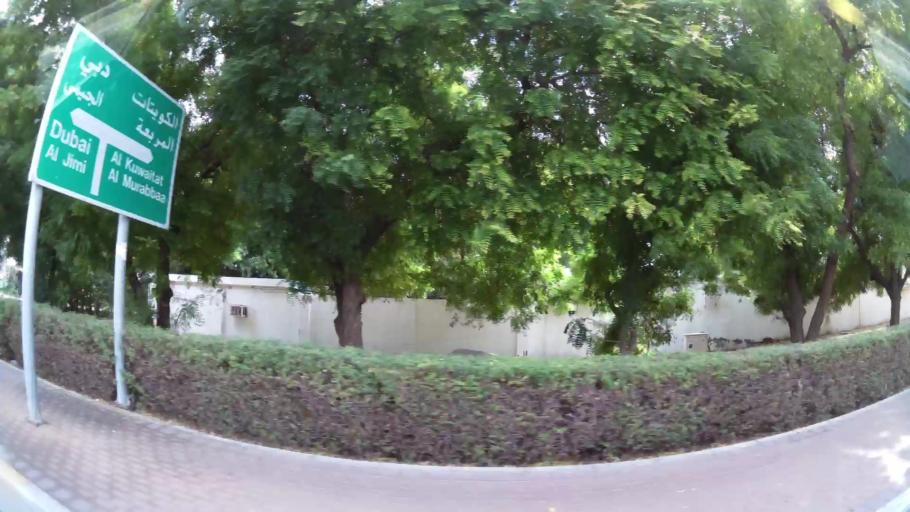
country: AE
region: Abu Dhabi
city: Al Ain
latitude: 24.2294
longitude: 55.7565
